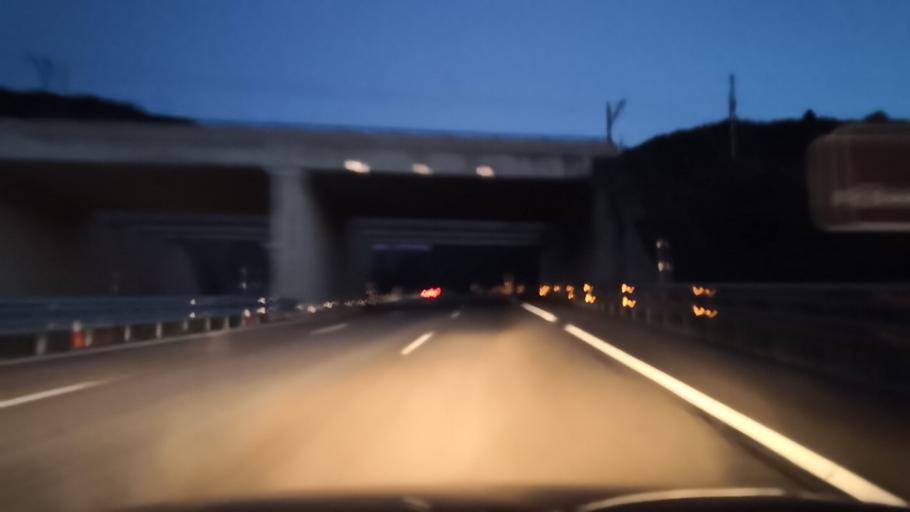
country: ES
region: Castille and Leon
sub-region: Provincia de Leon
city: Folgoso de la Ribera
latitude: 42.6088
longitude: -6.2701
